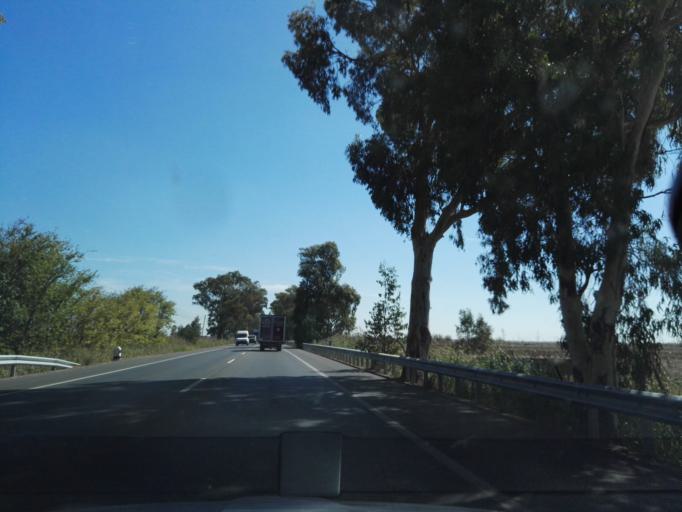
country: PT
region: Lisbon
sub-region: Vila Franca de Xira
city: Vila Franca de Xira
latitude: 38.9397
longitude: -8.9378
